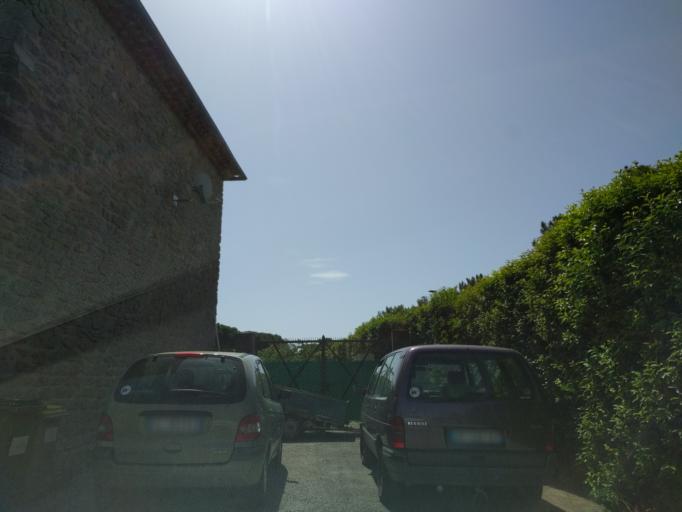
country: FR
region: Languedoc-Roussillon
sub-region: Departement de l'Aude
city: Carcassonne
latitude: 43.2124
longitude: 2.3730
